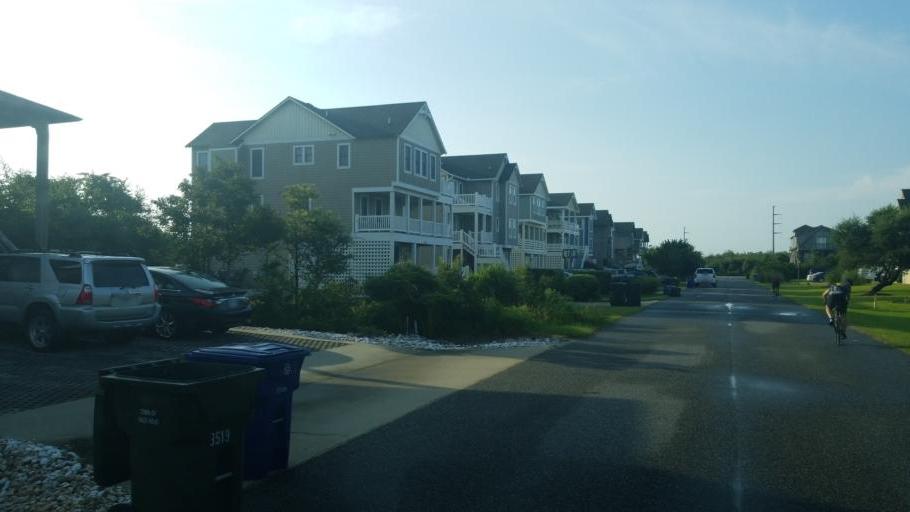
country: US
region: North Carolina
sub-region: Dare County
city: Nags Head
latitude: 35.9690
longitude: -75.6323
